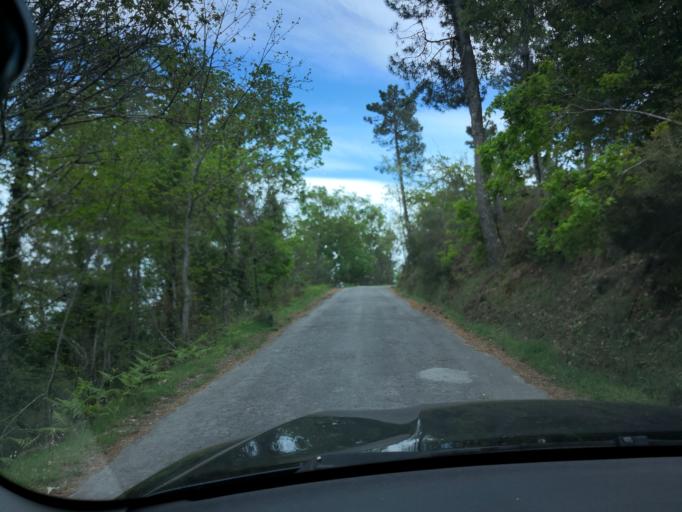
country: PT
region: Vila Real
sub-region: Vila Real
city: Vila Real
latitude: 41.2935
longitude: -7.8049
